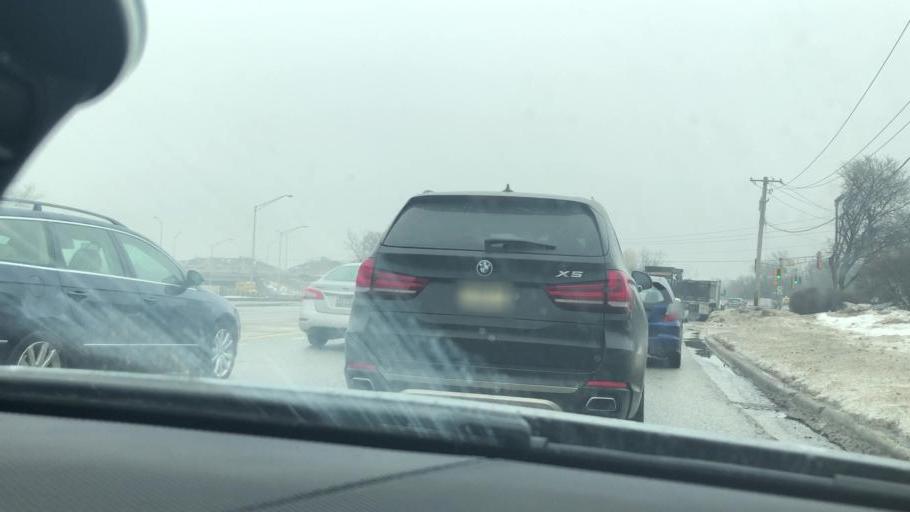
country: US
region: Illinois
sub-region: Cook County
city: Des Plaines
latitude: 42.0398
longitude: -87.8720
